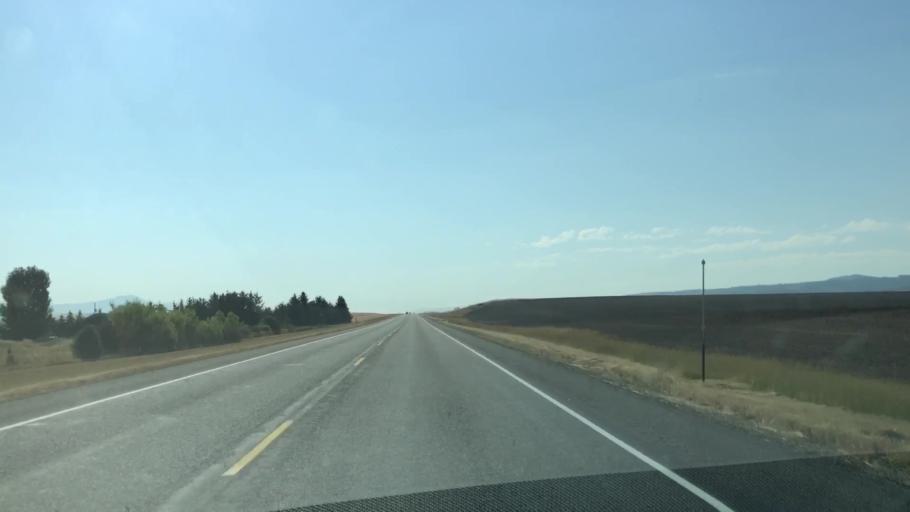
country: US
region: Idaho
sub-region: Madison County
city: Rexburg
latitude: 43.5708
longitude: -111.5567
